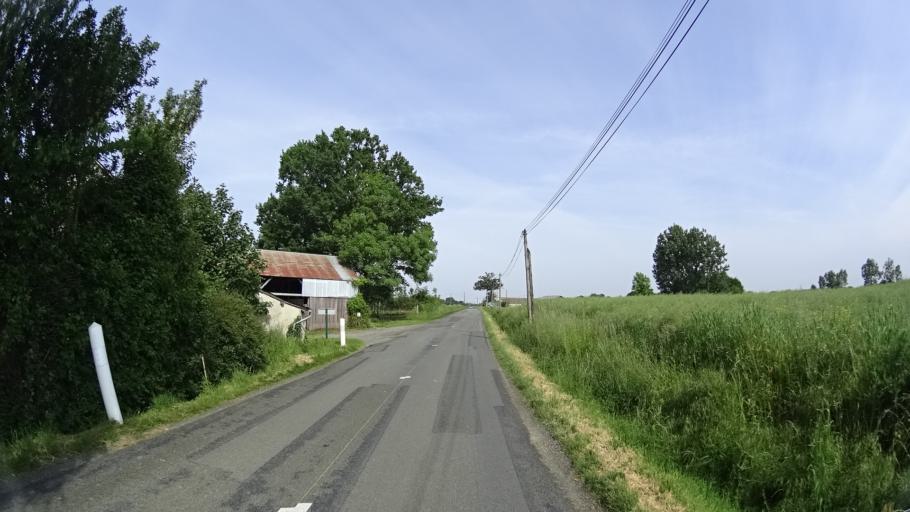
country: FR
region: Brittany
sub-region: Departement d'Ille-et-Vilaine
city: Chateaugiron
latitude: 48.0337
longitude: -1.5137
